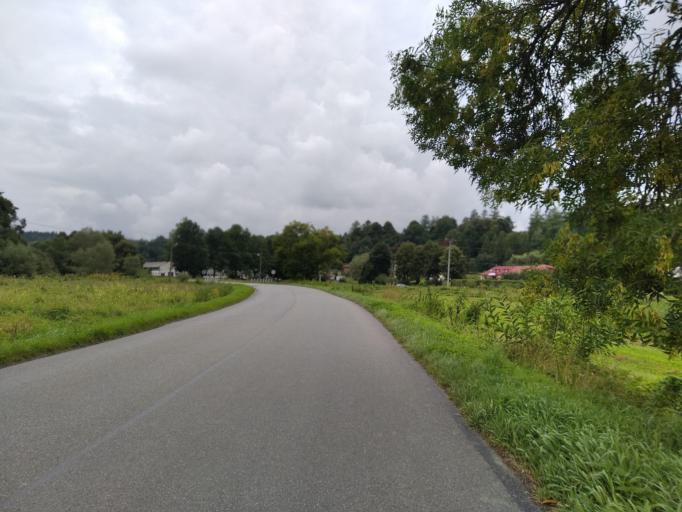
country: PL
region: Subcarpathian Voivodeship
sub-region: Powiat przemyski
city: Bircza
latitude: 49.7023
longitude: 22.3678
